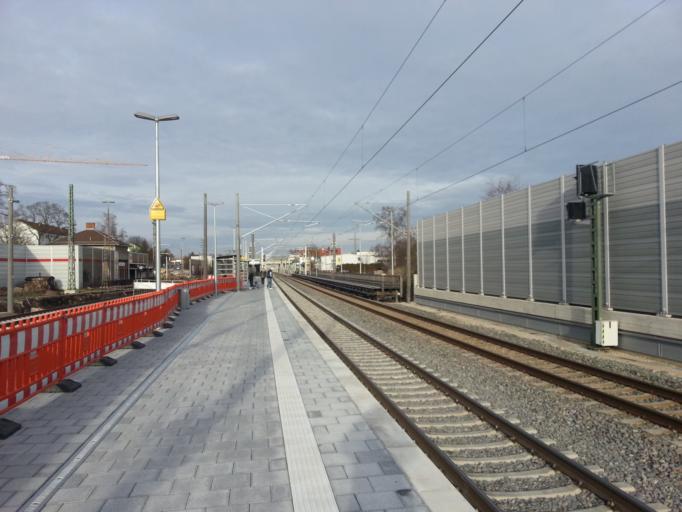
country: DE
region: Bavaria
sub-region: Regierungsbezirk Mittelfranken
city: Erlangen
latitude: 49.5693
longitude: 10.9969
